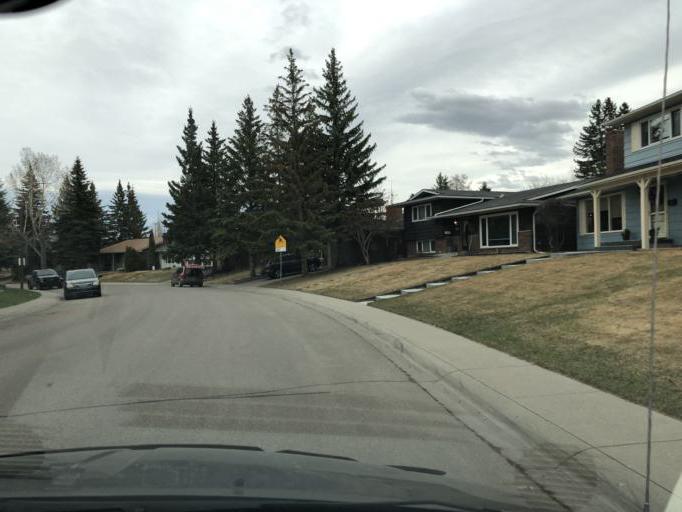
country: CA
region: Alberta
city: Calgary
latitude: 50.9321
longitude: -114.0422
